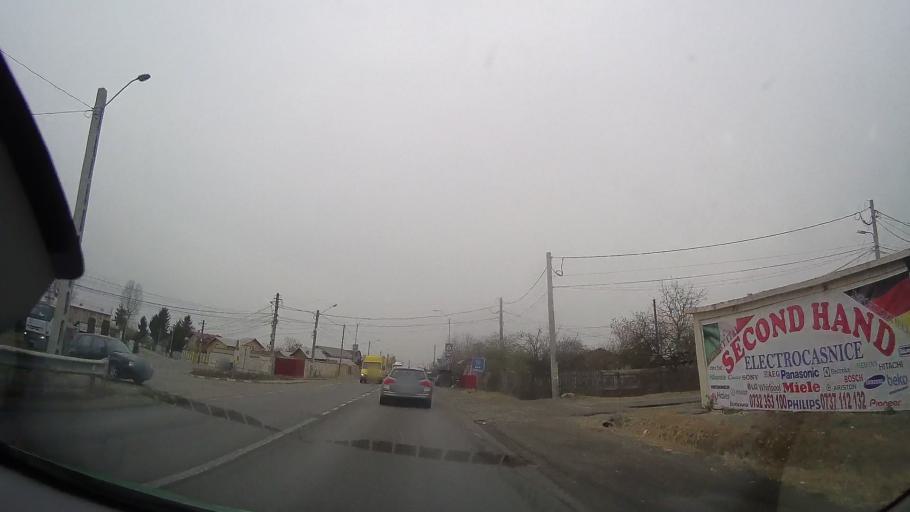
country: RO
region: Prahova
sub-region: Comuna Blejoiu
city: Ploiestiori
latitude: 44.9670
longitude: 26.0284
